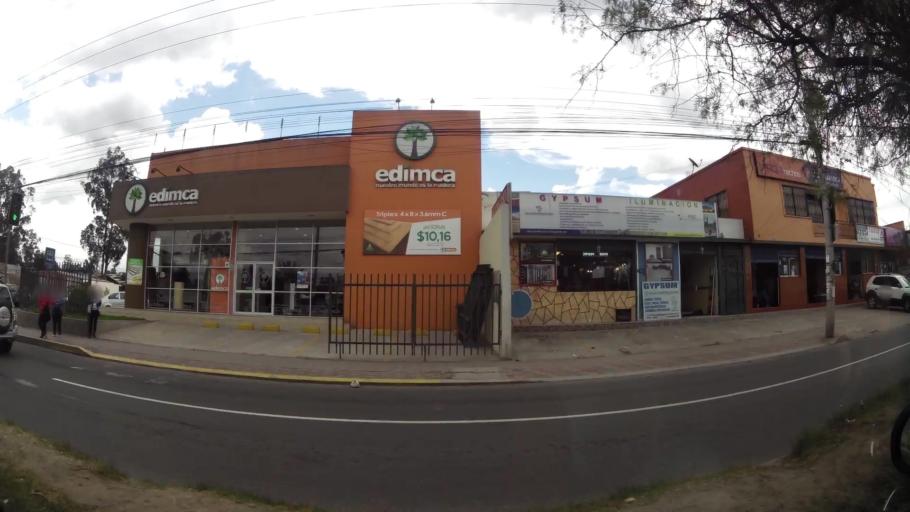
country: EC
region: Pichincha
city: Quito
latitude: -0.0891
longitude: -78.4279
